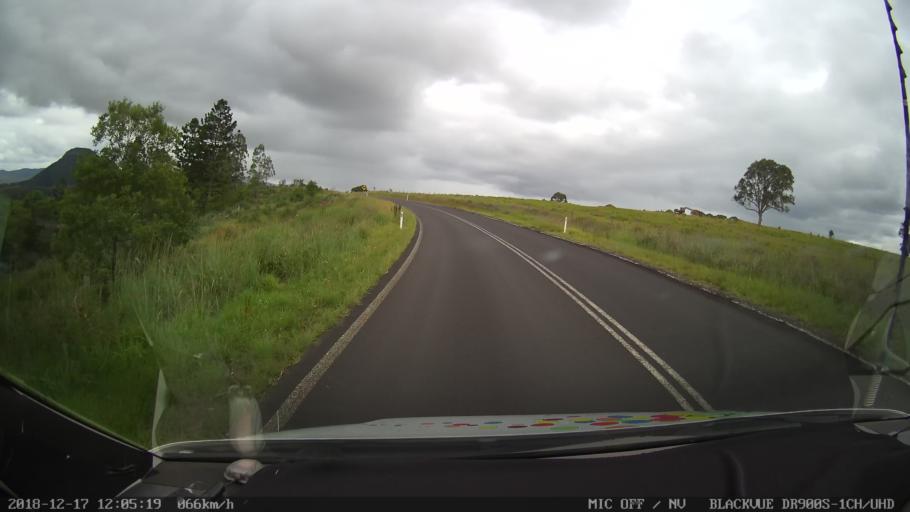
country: AU
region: New South Wales
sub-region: Kyogle
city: Kyogle
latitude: -28.4935
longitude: 152.5671
